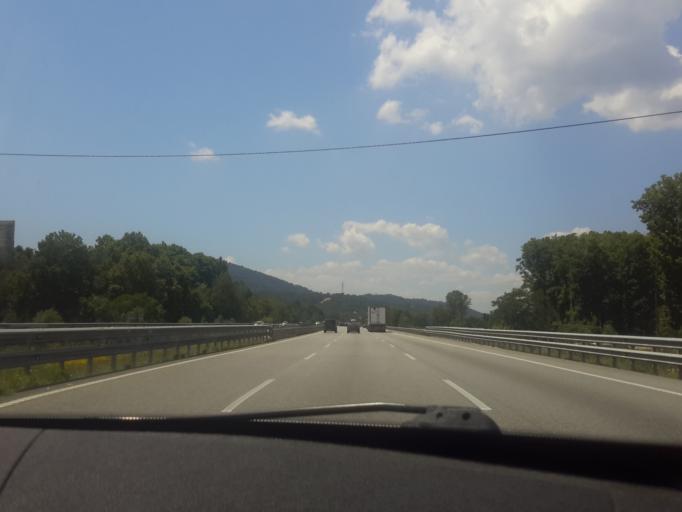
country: ES
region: Catalonia
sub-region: Provincia de Girona
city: Breda
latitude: 41.7217
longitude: 2.5737
